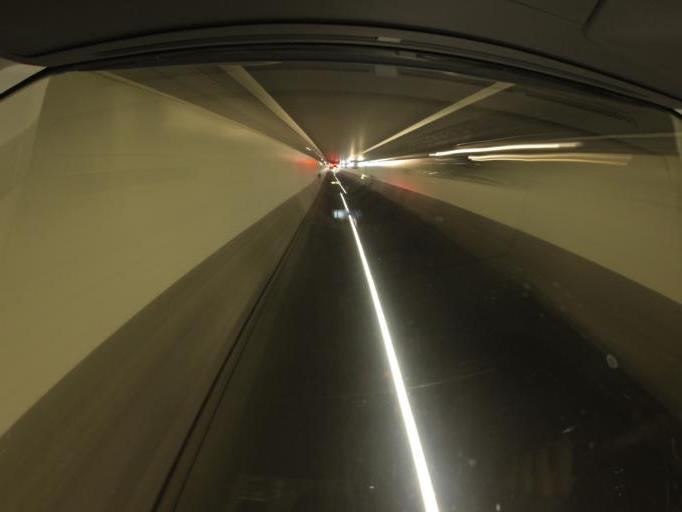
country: CH
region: Zurich
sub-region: Bezirk Hinwil
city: Rueti / Dorfzentrum, Suedl. Teil
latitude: 47.2366
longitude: 8.8649
